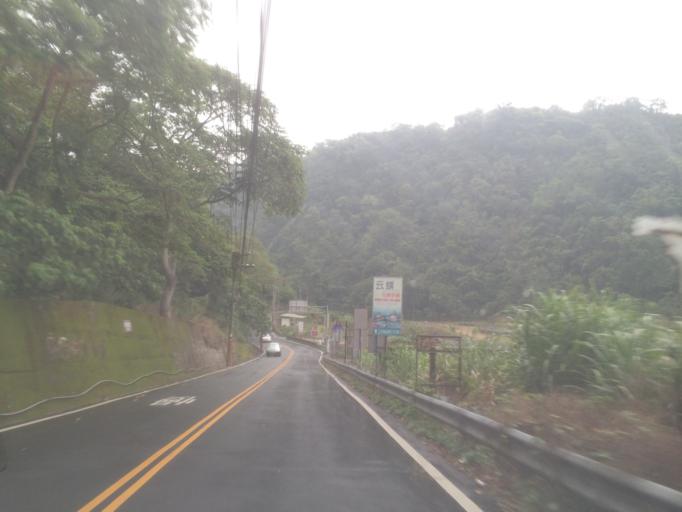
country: TW
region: Taiwan
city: Fengyuan
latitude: 24.1680
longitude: 120.8260
